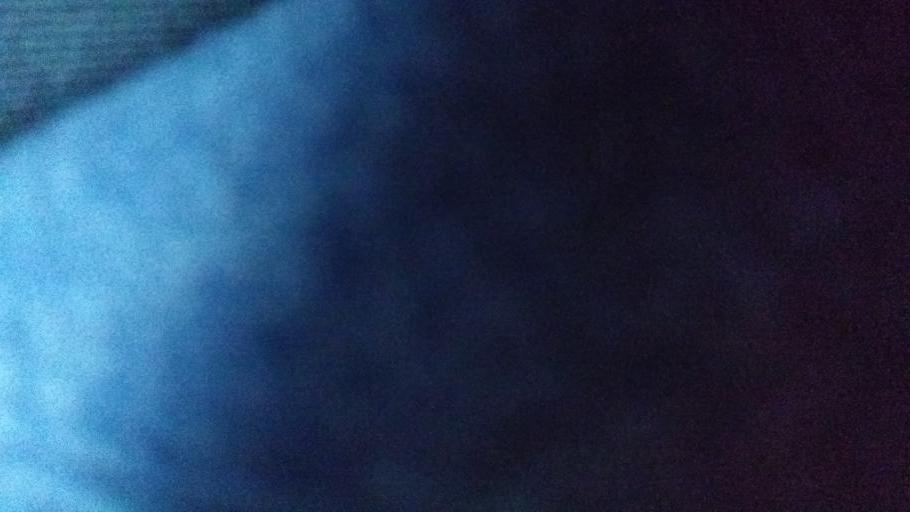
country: MX
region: Yucatan
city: Itzincab Palomeque
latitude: 20.9290
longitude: -89.6661
